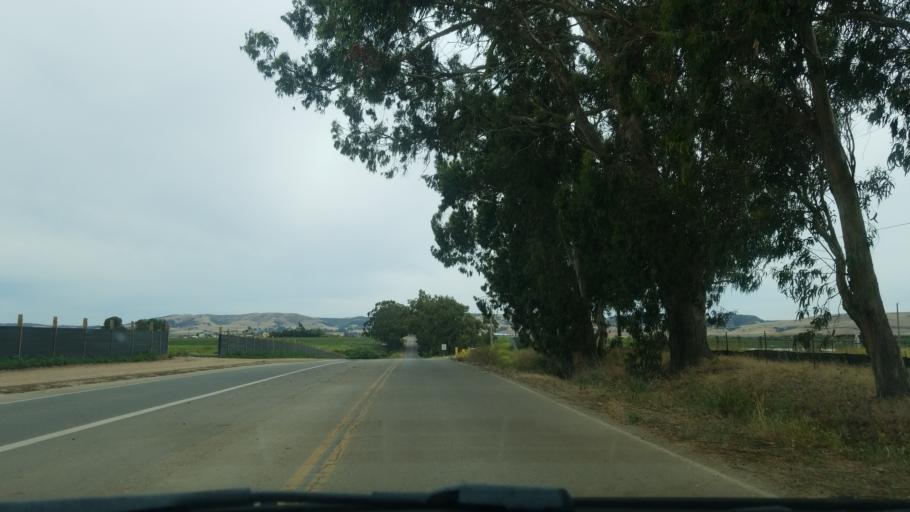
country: US
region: California
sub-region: Santa Barbara County
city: Santa Maria
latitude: 34.9178
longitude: -120.4902
